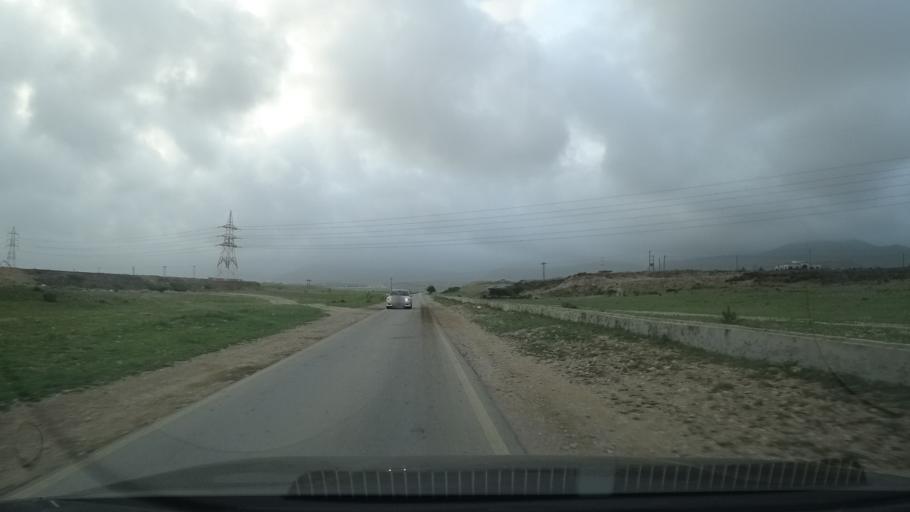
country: OM
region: Zufar
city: Salalah
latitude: 17.1028
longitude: 54.2324
